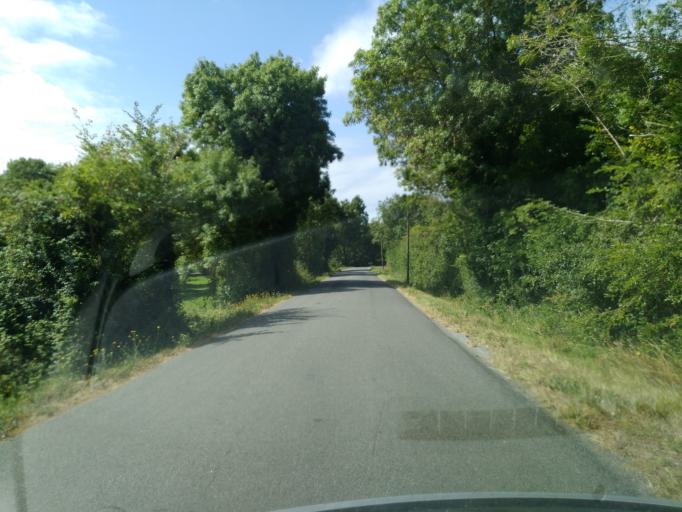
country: FR
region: Poitou-Charentes
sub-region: Departement de la Charente-Maritime
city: Breuillet
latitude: 45.6836
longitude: -1.0793
